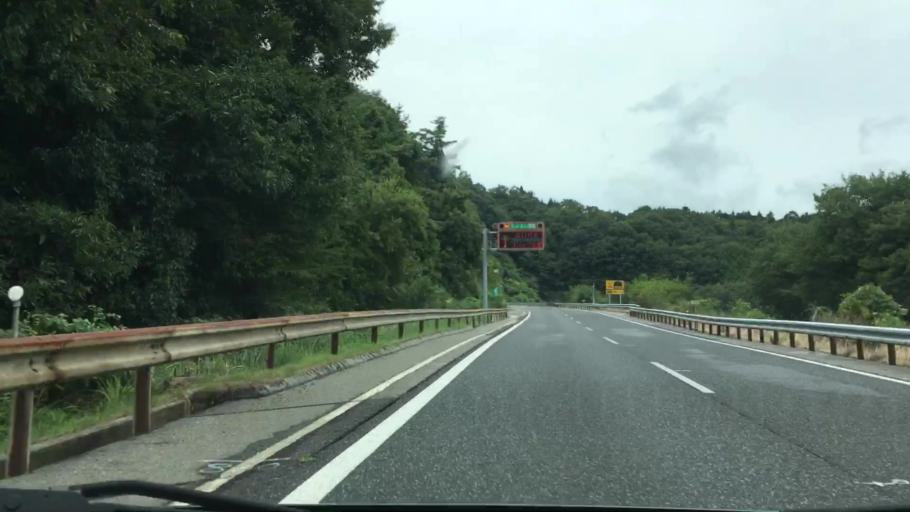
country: JP
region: Okayama
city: Niimi
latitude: 34.9812
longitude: 133.6153
